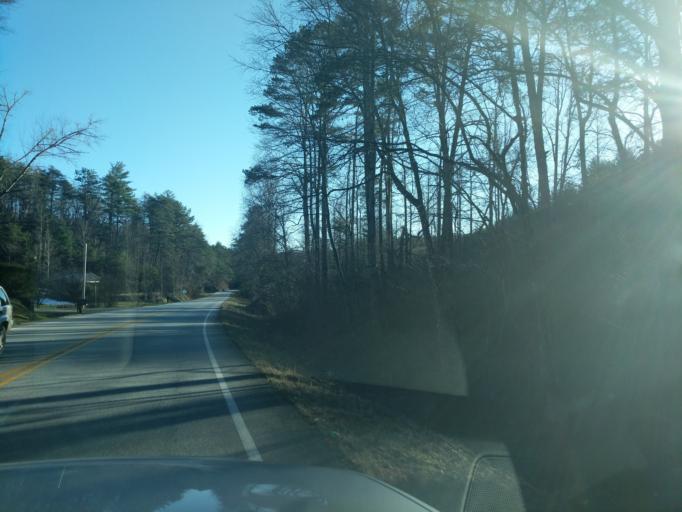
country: US
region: Georgia
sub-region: Rabun County
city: Clayton
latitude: 34.8213
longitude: -83.3196
